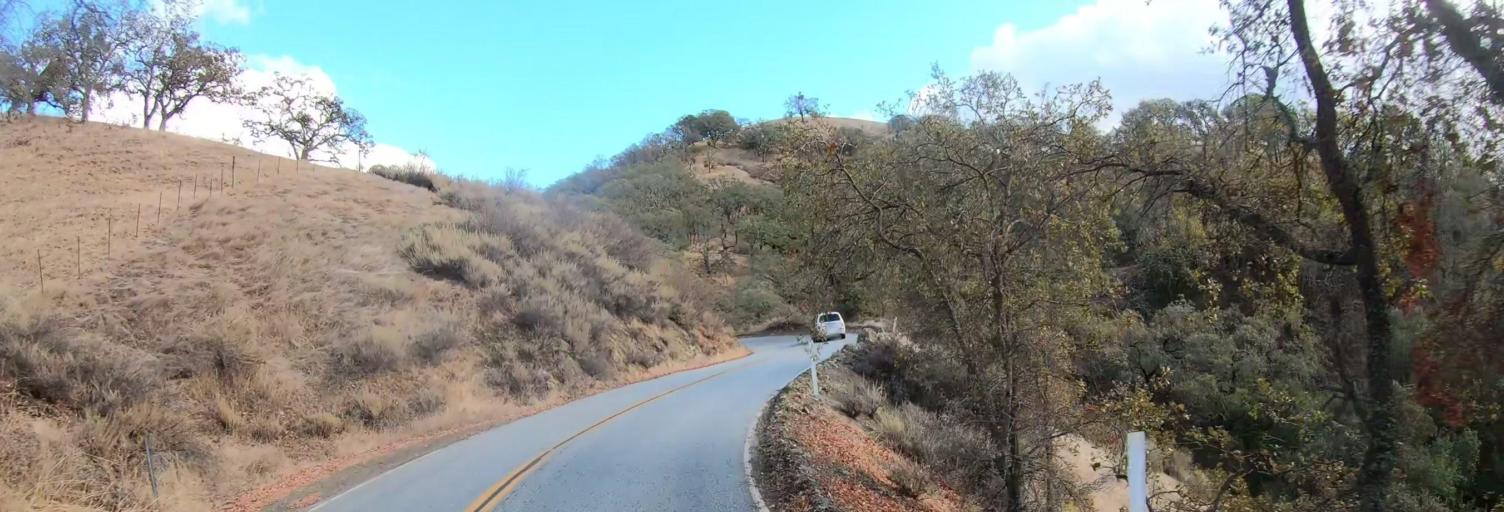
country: US
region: California
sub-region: Santa Clara County
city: East Foothills
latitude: 37.3343
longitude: -121.6977
